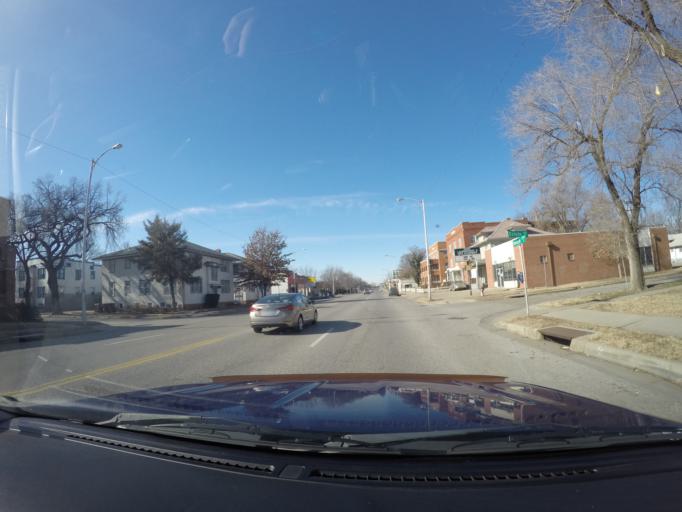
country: US
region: Kansas
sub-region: Sedgwick County
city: Wichita
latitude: 37.6863
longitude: -97.3045
